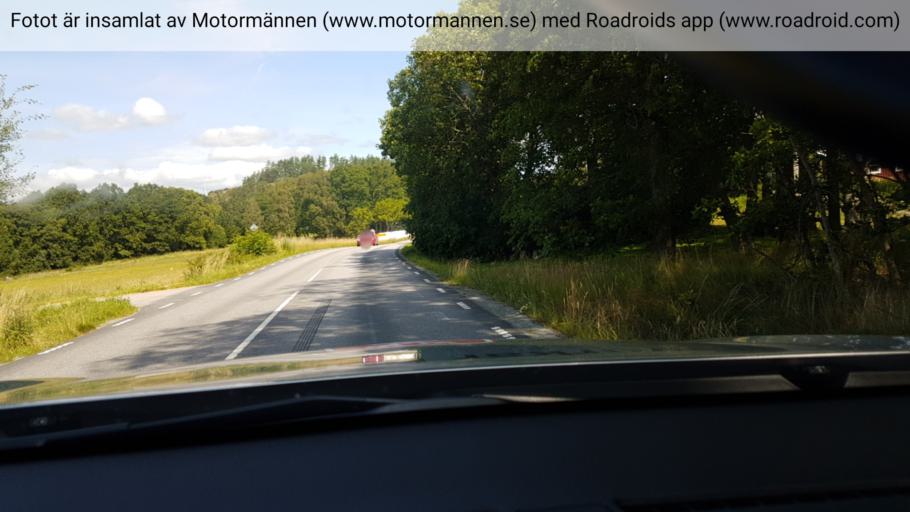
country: SE
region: Vaestra Goetaland
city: Svanesund
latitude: 58.1192
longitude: 11.8544
